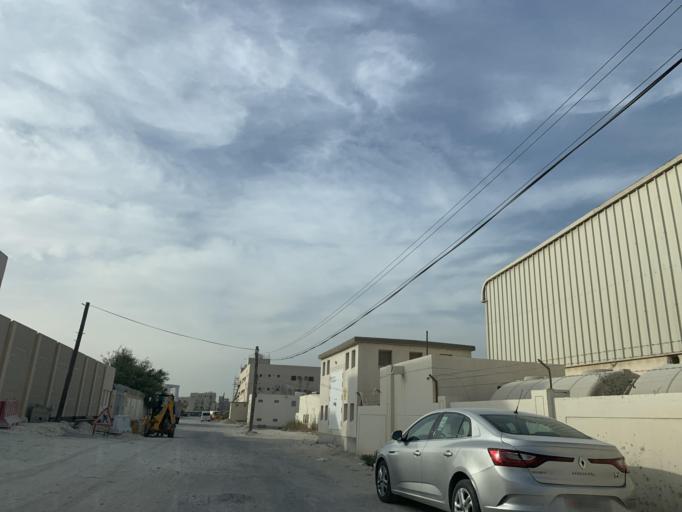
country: BH
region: Northern
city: Ar Rifa'
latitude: 26.1264
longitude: 50.5856
